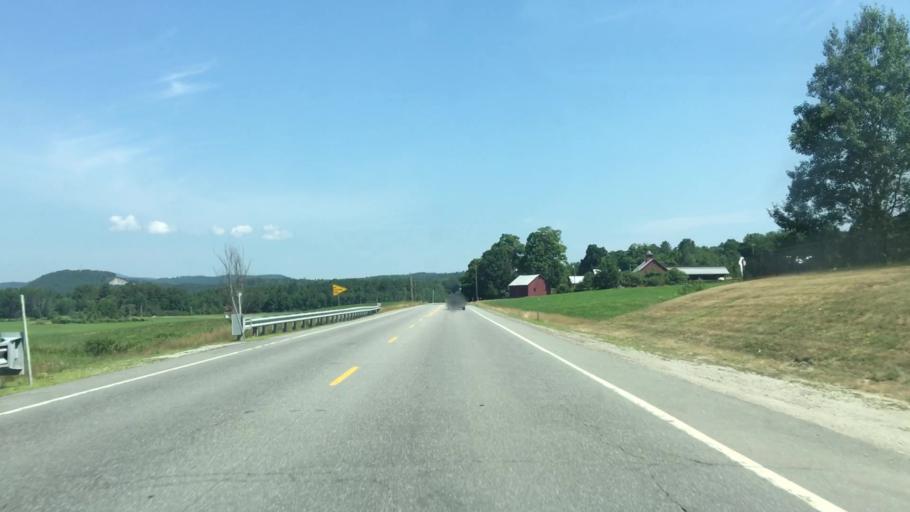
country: US
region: New Hampshire
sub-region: Sullivan County
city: Sunapee
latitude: 43.3600
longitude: -72.1196
